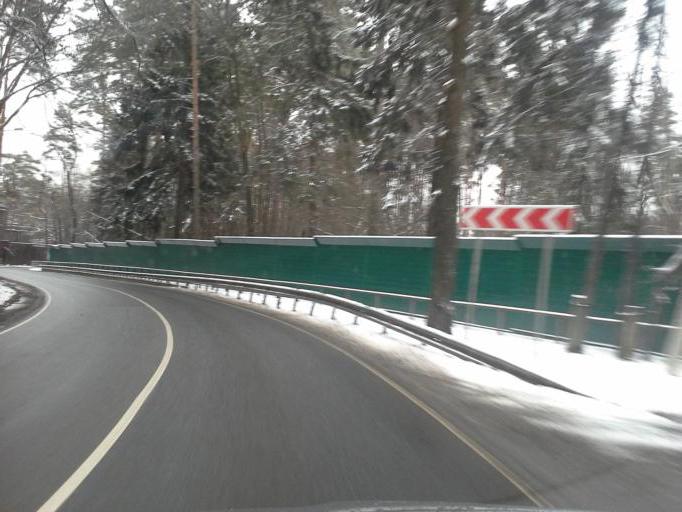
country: RU
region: Moskovskaya
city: Nikolina Gora
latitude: 55.7257
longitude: 37.0513
